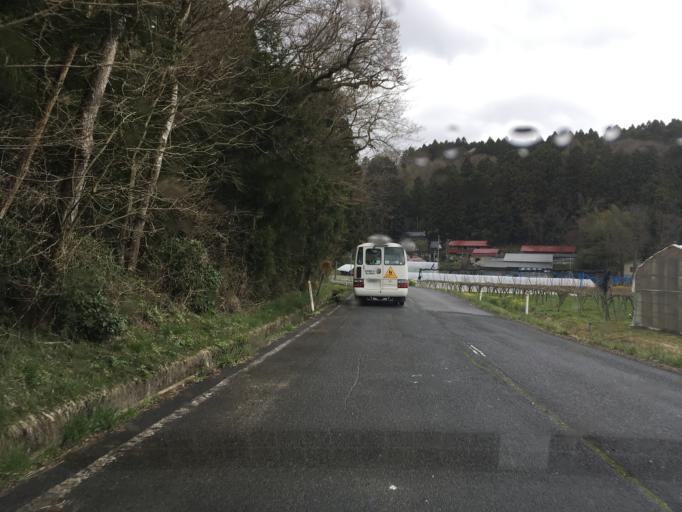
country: JP
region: Iwate
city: Ichinoseki
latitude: 38.7510
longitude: 141.2258
